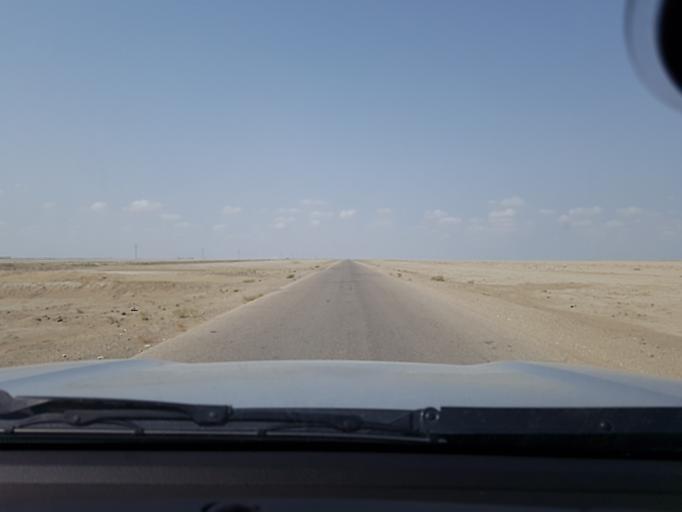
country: TM
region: Balkan
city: Gumdag
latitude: 38.6527
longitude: 54.3873
